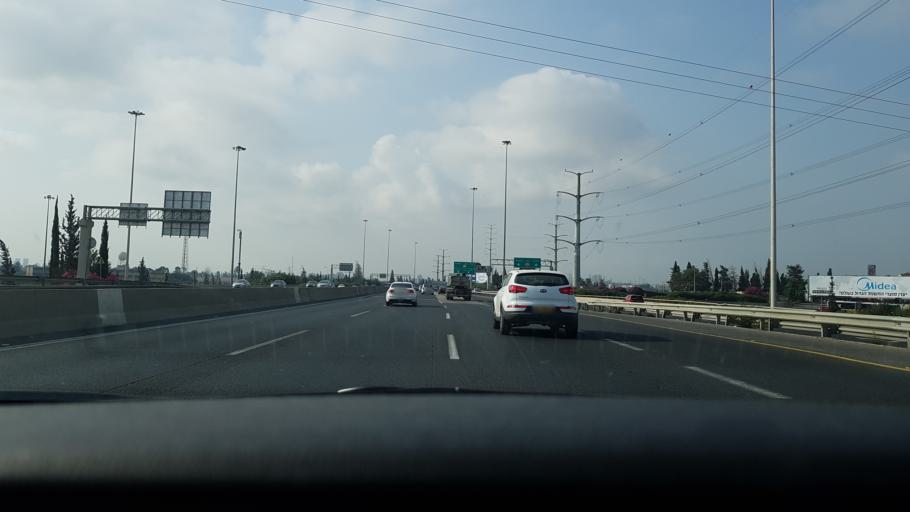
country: IL
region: Tel Aviv
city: Azor
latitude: 32.0115
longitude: 34.8150
